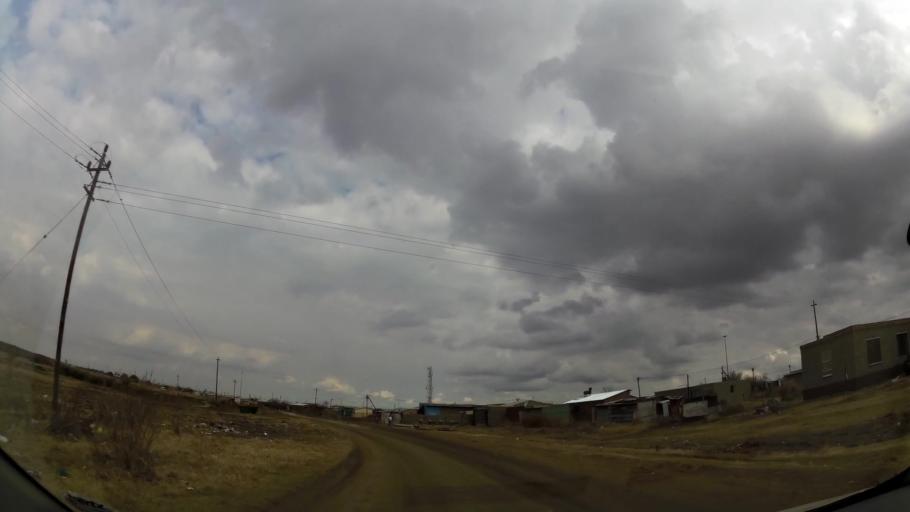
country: ZA
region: Orange Free State
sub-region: Fezile Dabi District Municipality
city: Sasolburg
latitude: -26.8772
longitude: 27.8749
